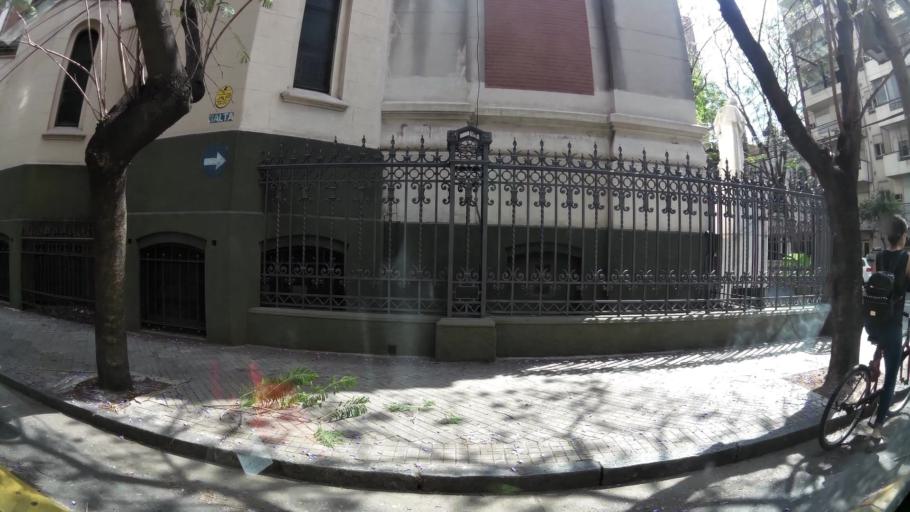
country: AR
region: Santa Fe
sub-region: Departamento de Rosario
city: Rosario
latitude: -32.9383
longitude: -60.6435
